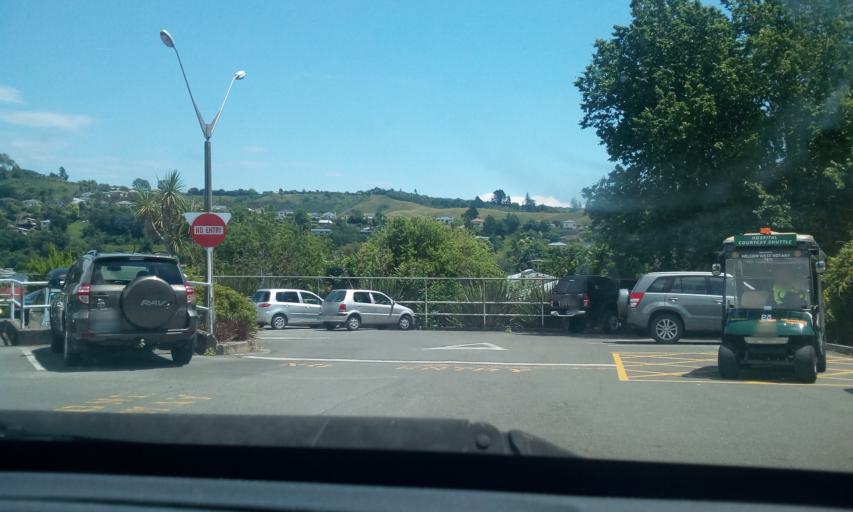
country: NZ
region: Nelson
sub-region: Nelson City
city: Nelson
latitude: -41.2868
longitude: 173.2717
